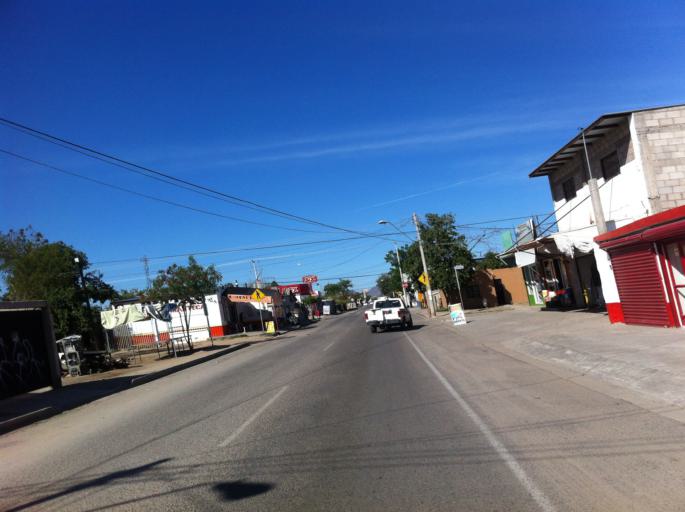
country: MX
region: Sonora
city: Hermosillo
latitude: 29.1068
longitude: -111.0113
